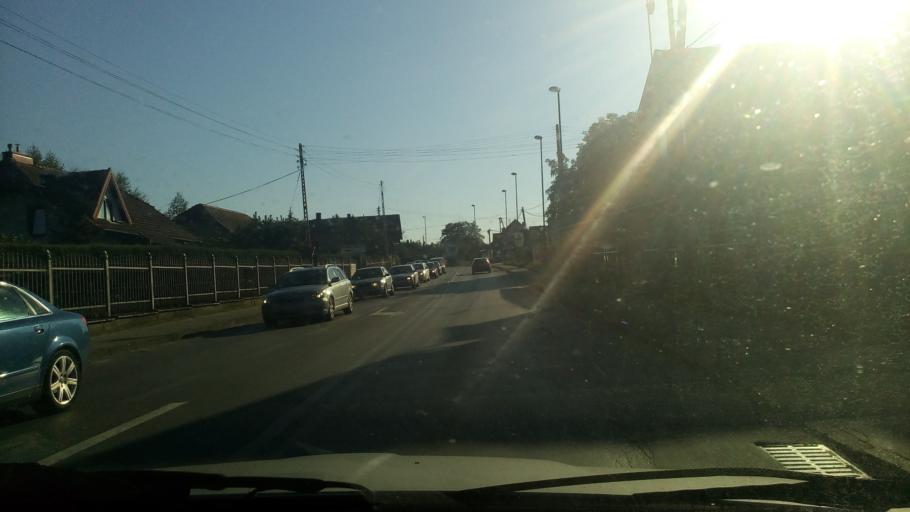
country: PL
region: Lesser Poland Voivodeship
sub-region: Powiat nowosadecki
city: Stary Sacz
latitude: 49.5809
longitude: 20.6681
